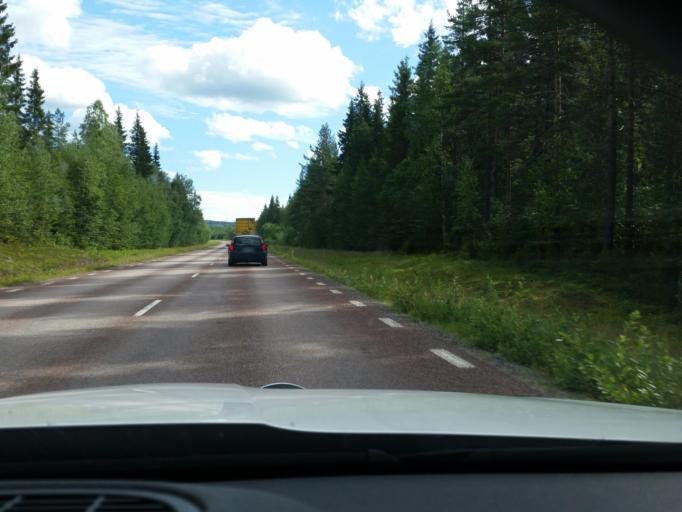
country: SE
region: Norrbotten
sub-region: Alvsbyns Kommun
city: AElvsbyn
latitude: 65.6728
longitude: 21.1659
